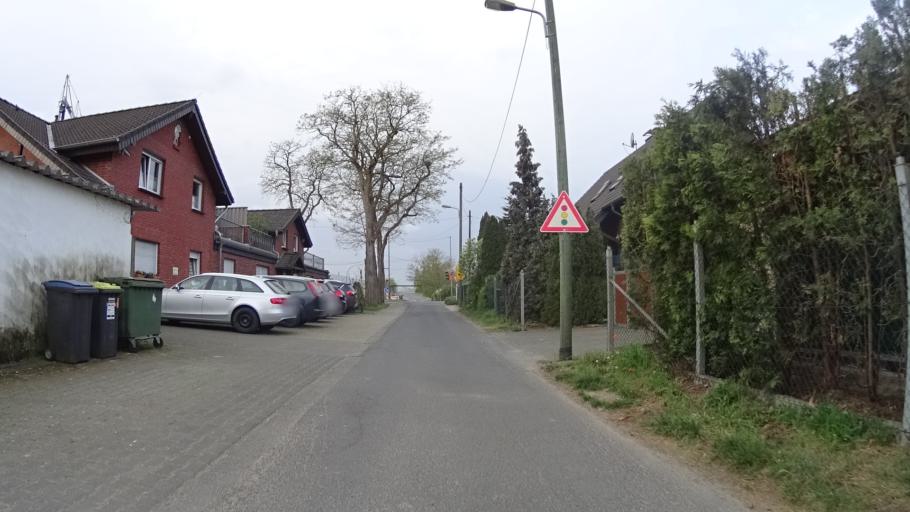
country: DE
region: North Rhine-Westphalia
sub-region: Regierungsbezirk Koln
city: Leverkusen
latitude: 51.0311
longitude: 6.9525
